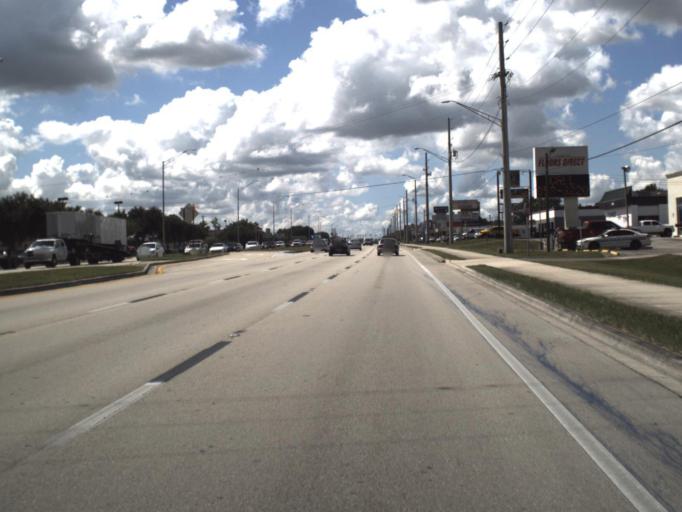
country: US
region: Florida
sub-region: Polk County
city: Gibsonia
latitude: 28.1073
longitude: -81.9738
